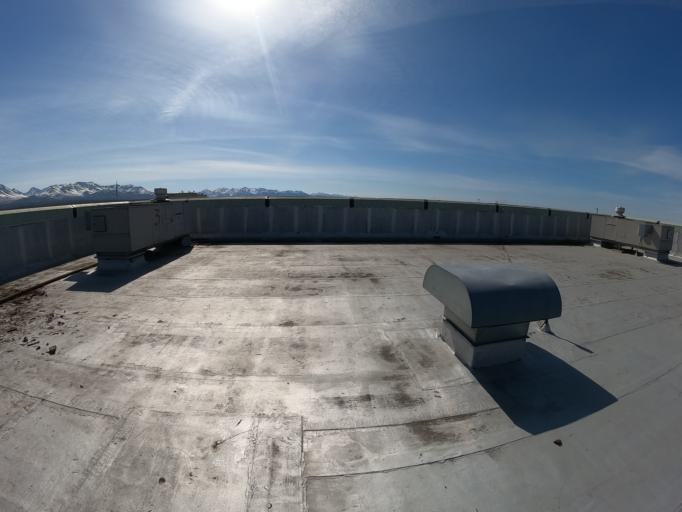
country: US
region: Alaska
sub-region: Anchorage Municipality
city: Anchorage
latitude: 61.1466
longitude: -149.8712
